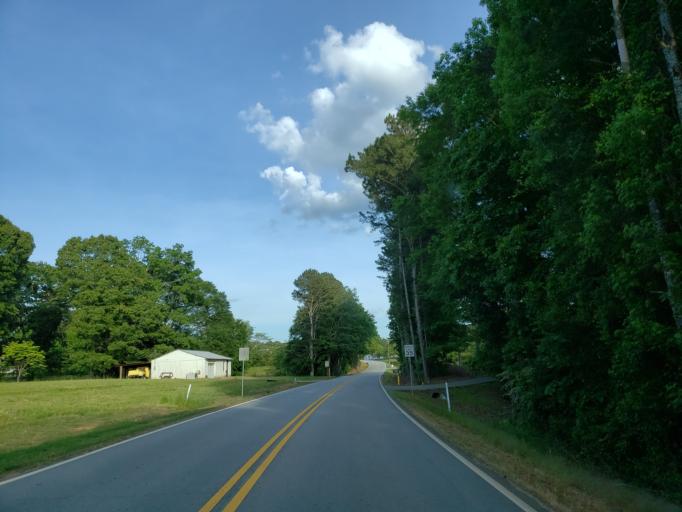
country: US
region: Georgia
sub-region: Carroll County
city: Mount Zion
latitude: 33.6361
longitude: -85.1906
